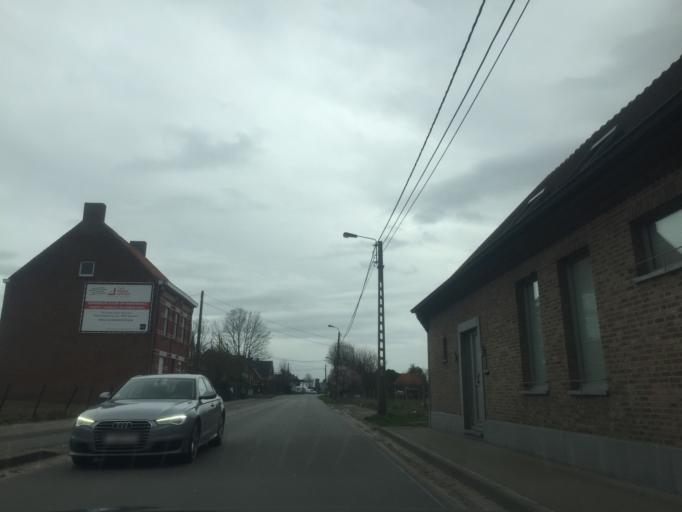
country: BE
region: Flanders
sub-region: Provincie West-Vlaanderen
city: Ardooie
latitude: 50.9715
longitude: 3.1960
